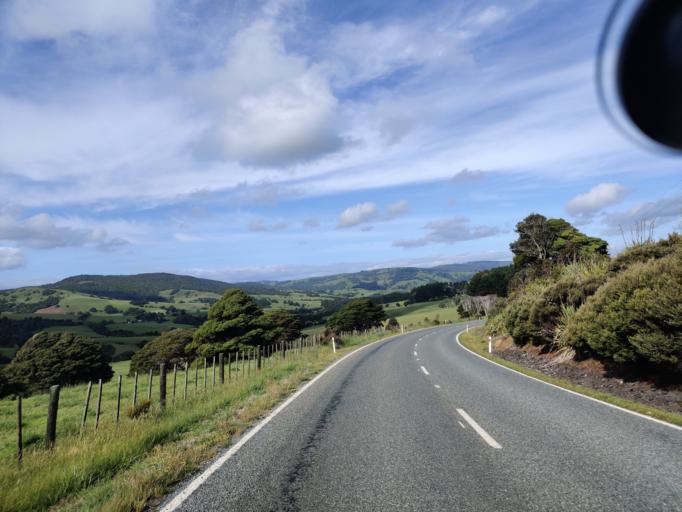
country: NZ
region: Northland
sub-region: Kaipara District
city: Dargaville
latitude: -35.7173
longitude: 173.5806
